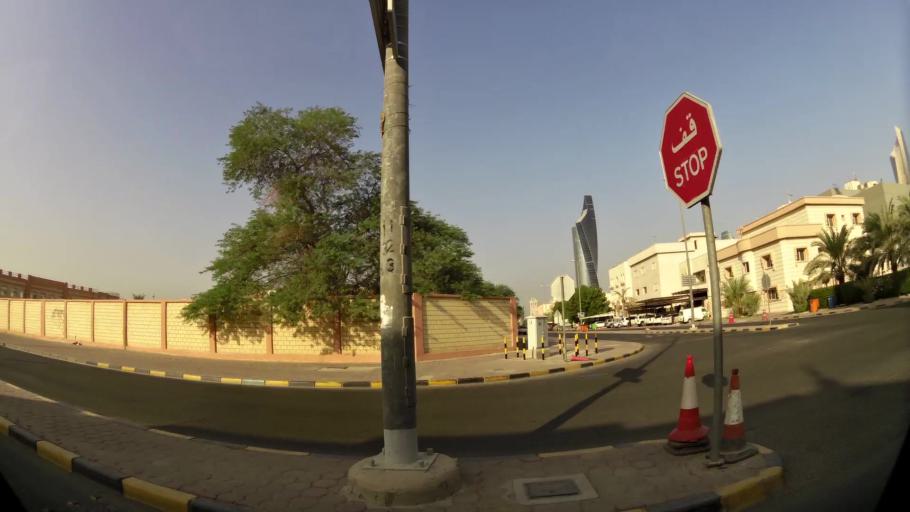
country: KW
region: Al Asimah
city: Ad Dasmah
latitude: 29.3684
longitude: 48.0001
